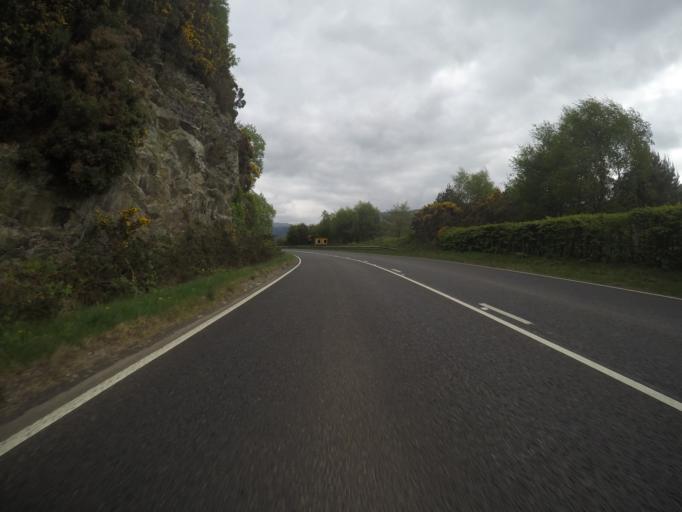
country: GB
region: Scotland
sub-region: Highland
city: Fort William
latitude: 57.2729
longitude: -5.5123
